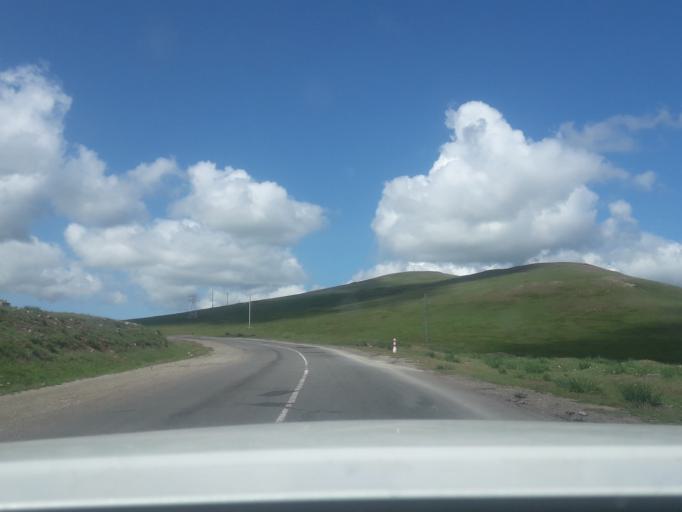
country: MN
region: Central Aimak
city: Ihsueuej
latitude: 48.1279
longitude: 106.4320
